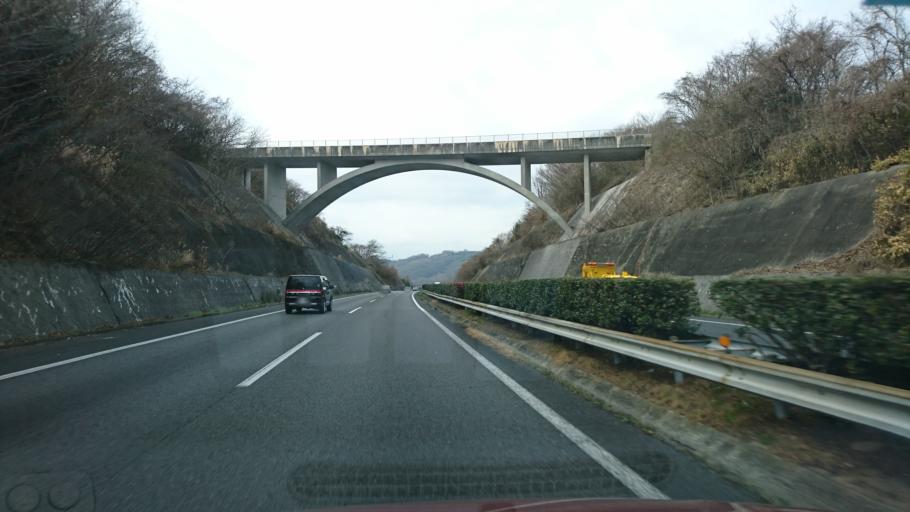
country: JP
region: Okayama
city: Kurashiki
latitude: 34.6044
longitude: 133.7207
